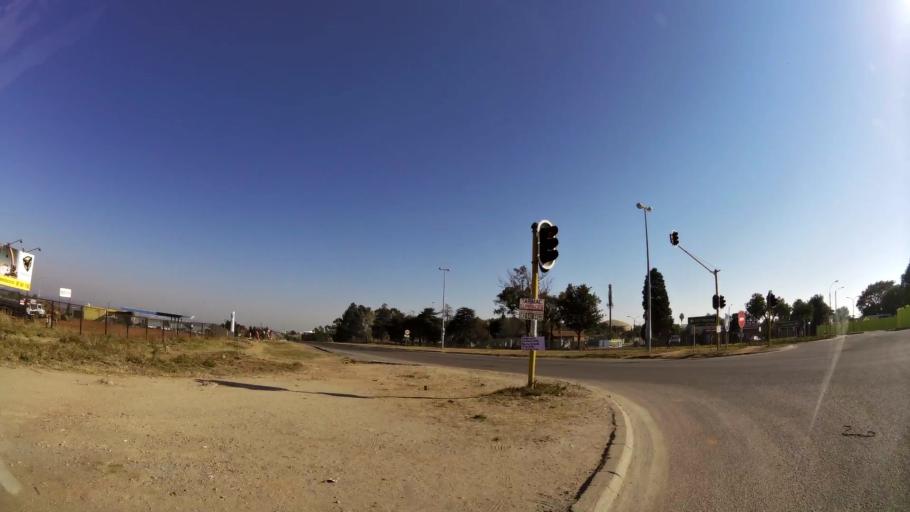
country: ZA
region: Gauteng
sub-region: City of Johannesburg Metropolitan Municipality
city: Modderfontein
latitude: -26.0604
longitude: 28.1771
